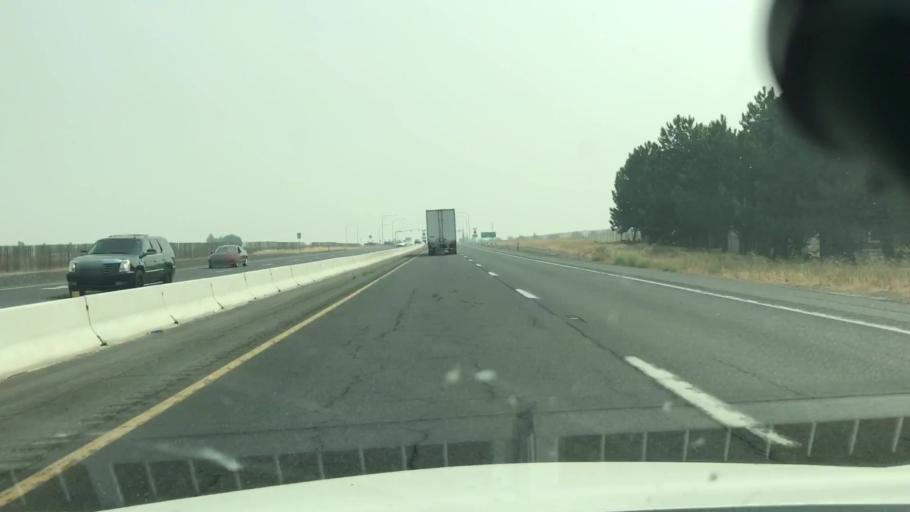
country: US
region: Washington
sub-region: Grant County
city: Cascade Valley
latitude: 47.1584
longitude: -119.3165
